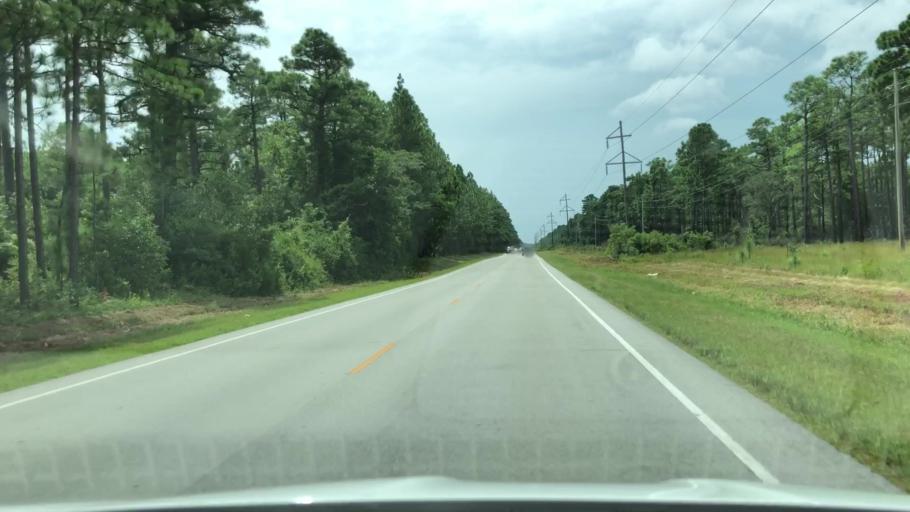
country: US
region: North Carolina
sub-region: Carteret County
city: Newport
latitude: 34.7630
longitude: -76.8699
